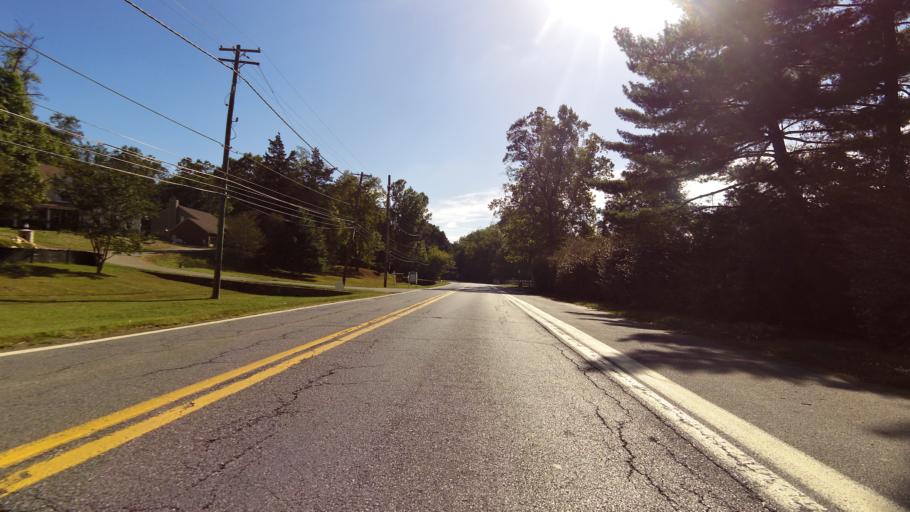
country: US
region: Maryland
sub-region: Montgomery County
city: Potomac
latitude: 38.9807
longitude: -77.2224
